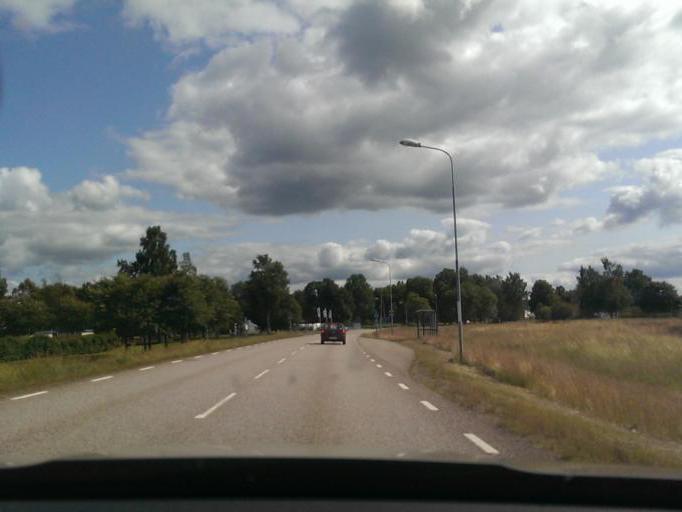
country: SE
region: Kronoberg
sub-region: Ljungby Kommun
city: Lagan
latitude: 56.9202
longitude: 13.9898
